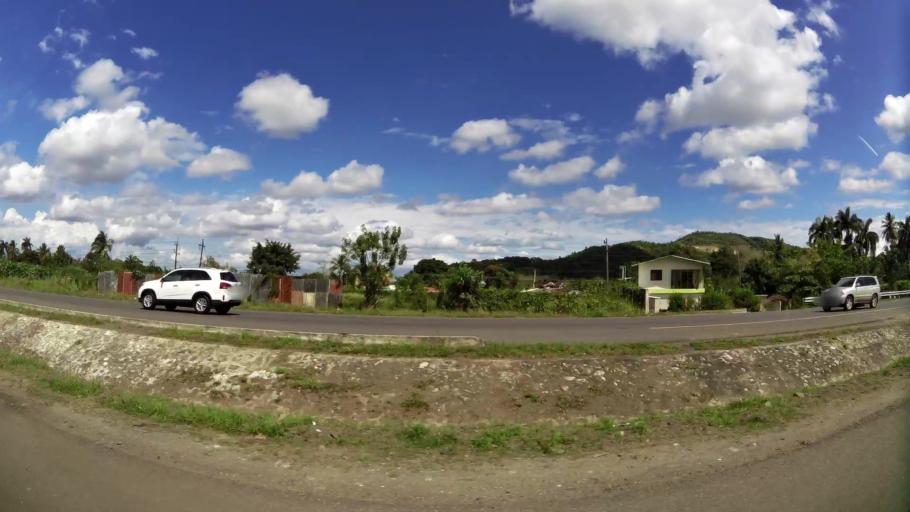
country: DO
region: La Vega
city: Rio Verde Arriba
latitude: 19.3094
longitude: -70.5855
